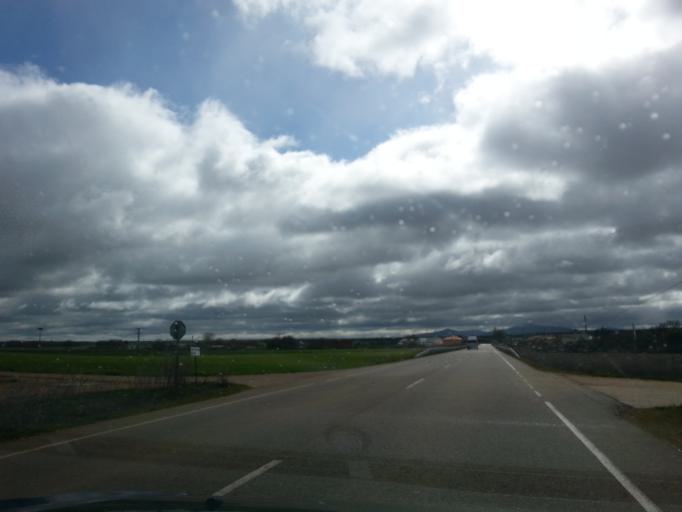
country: ES
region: Castille and Leon
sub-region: Provincia de Salamanca
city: Cabrillas
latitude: 40.7458
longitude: -6.1813
